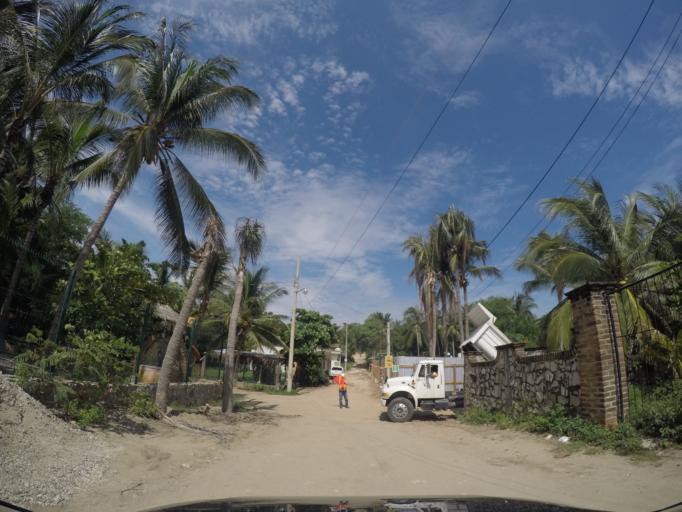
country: MX
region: Oaxaca
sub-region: Santa Maria Colotepec
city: Brisas de Zicatela
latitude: 15.8325
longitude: -97.0445
